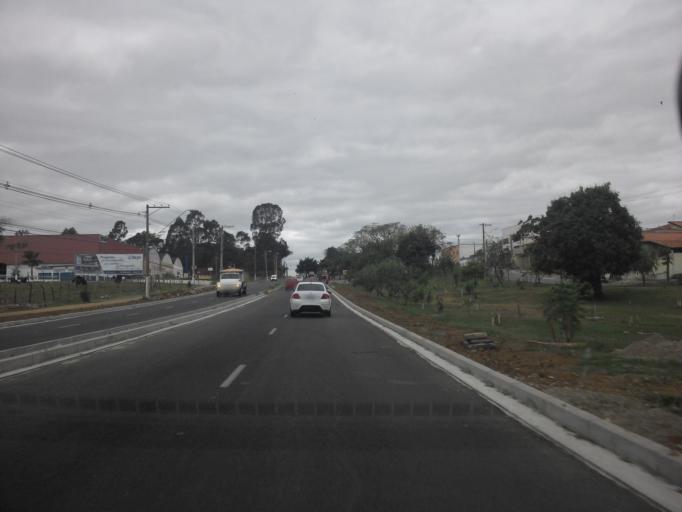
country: BR
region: Sao Paulo
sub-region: Taubate
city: Taubate
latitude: -23.0273
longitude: -45.6094
